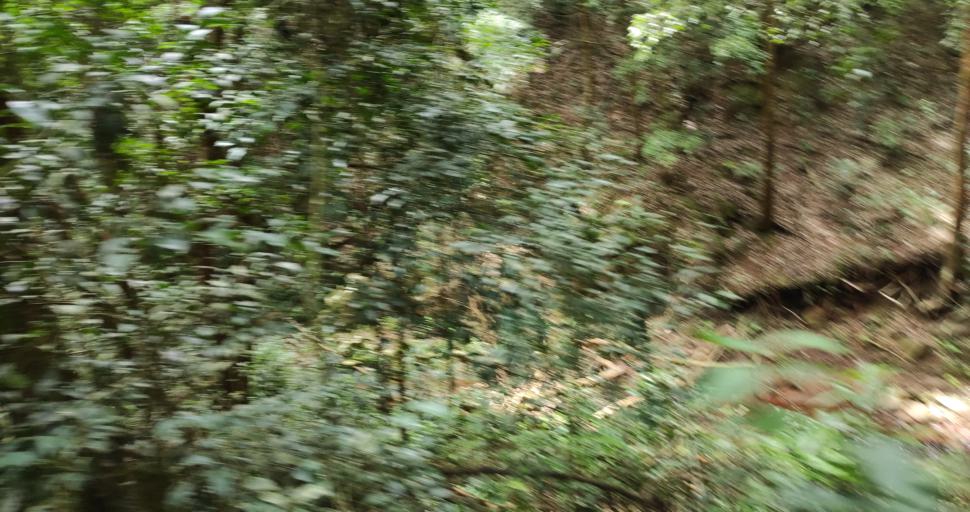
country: AR
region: Misiones
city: El Soberbio
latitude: -27.2749
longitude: -54.2202
